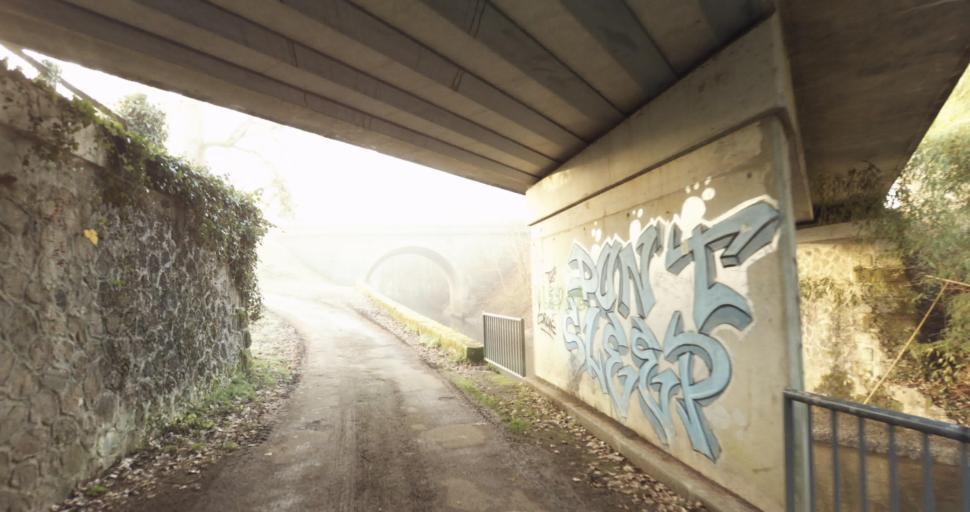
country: FR
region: Limousin
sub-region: Departement de la Haute-Vienne
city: Aixe-sur-Vienne
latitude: 45.7955
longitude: 1.1505
